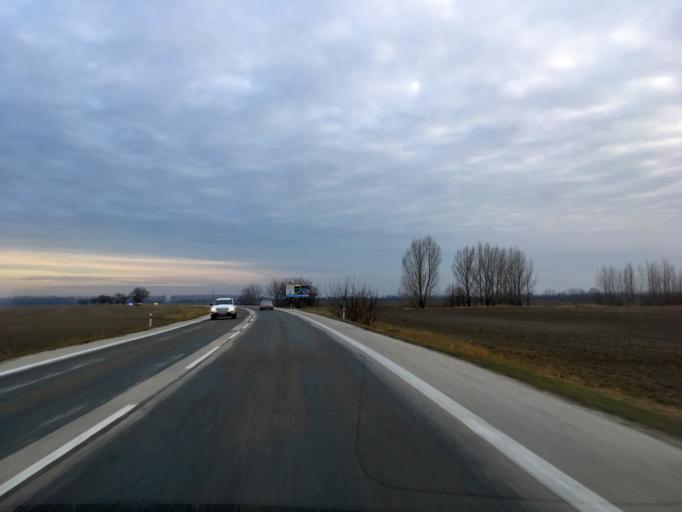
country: SK
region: Trnavsky
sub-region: Okres Dunajska Streda
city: Velky Meder
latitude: 47.9278
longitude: 17.7227
